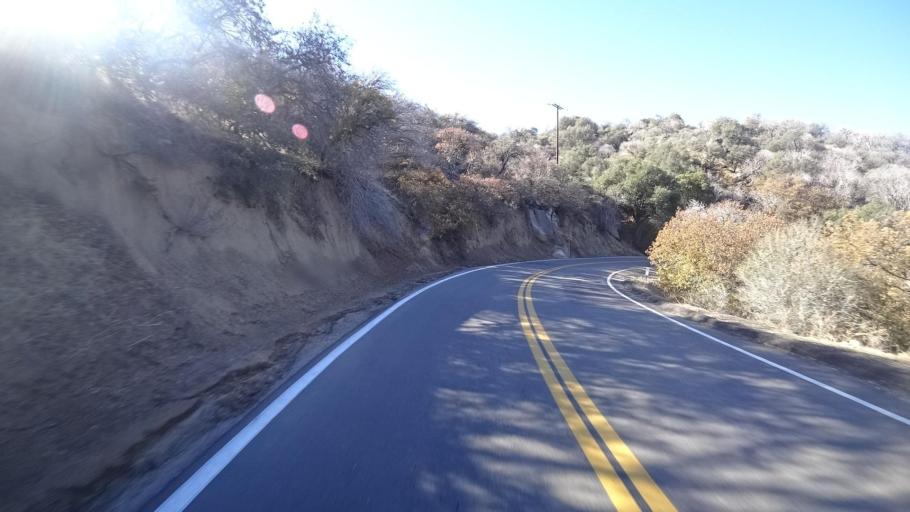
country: US
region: California
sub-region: Kern County
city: Alta Sierra
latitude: 35.7369
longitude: -118.6458
